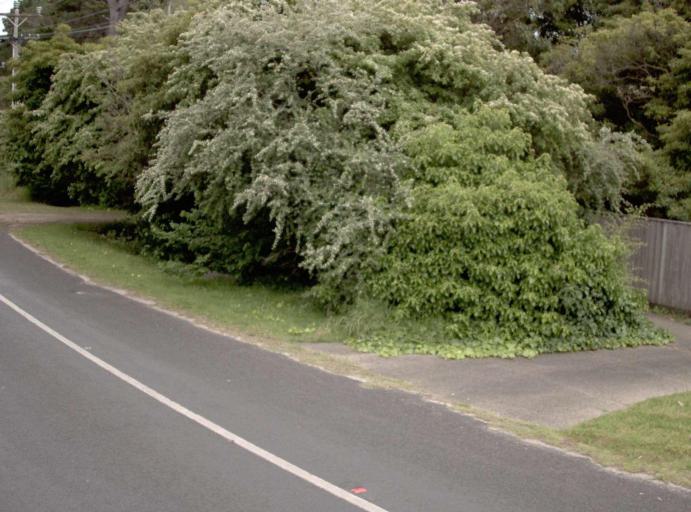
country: AU
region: Victoria
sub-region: Mornington Peninsula
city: Sorrento
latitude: -38.3330
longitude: 144.7382
